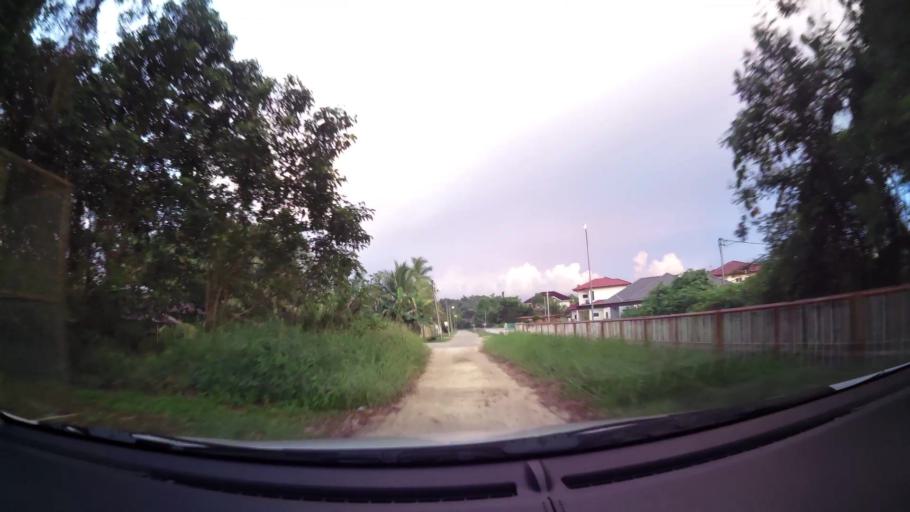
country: BN
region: Brunei and Muara
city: Bandar Seri Begawan
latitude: 4.9994
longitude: 114.9972
